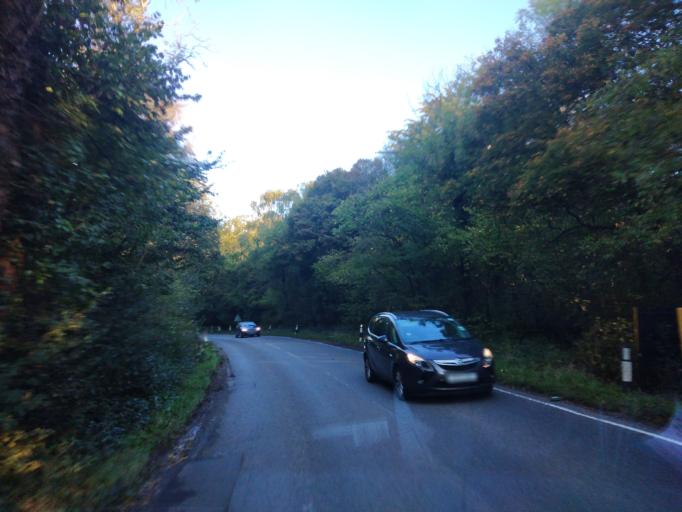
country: GB
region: England
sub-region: West Sussex
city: Goring-by-Sea
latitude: 50.8344
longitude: -0.4378
